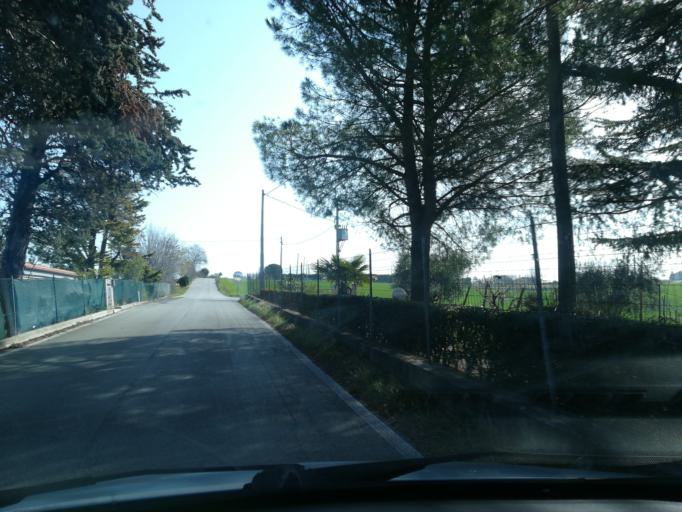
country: IT
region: The Marches
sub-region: Provincia di Macerata
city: Villa Potenza
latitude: 43.3315
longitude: 13.4580
